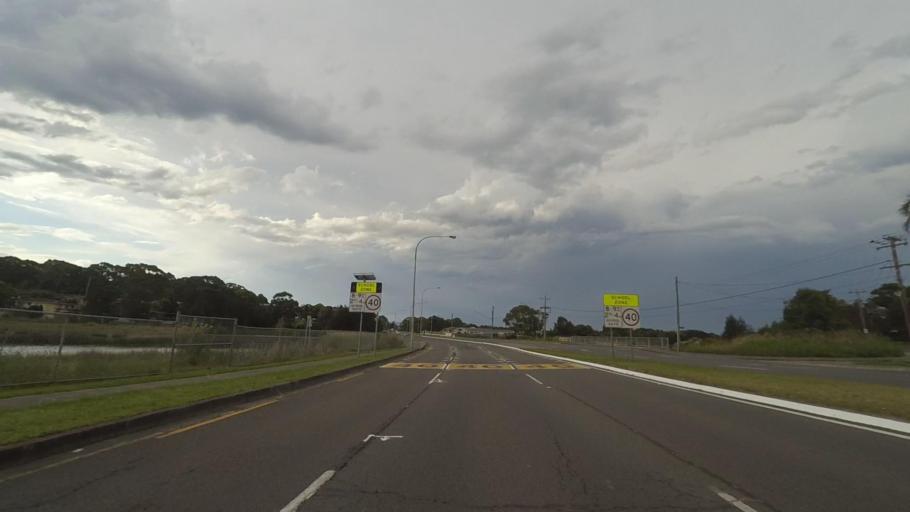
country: AU
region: New South Wales
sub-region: Shellharbour
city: Shellharbour Village
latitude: -34.5756
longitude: 150.8640
